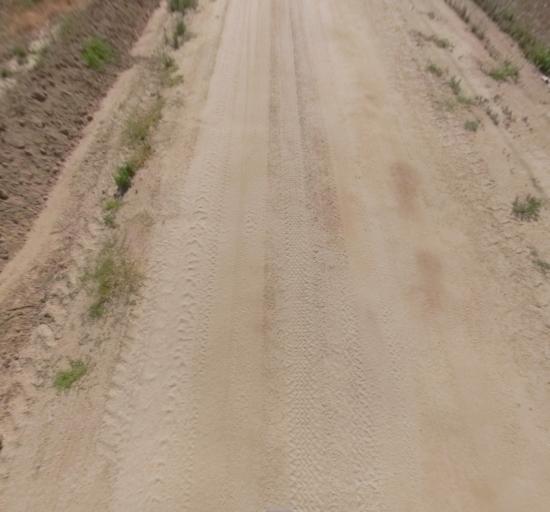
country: US
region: California
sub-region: Madera County
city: Chowchilla
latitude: 37.0108
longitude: -120.3693
